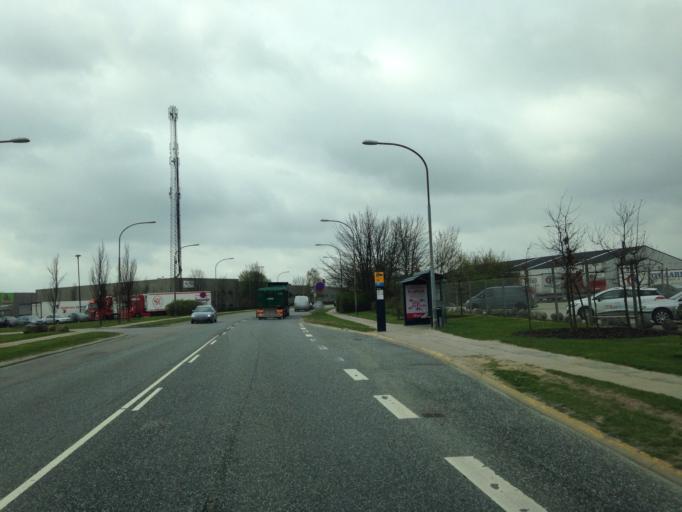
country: DK
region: Capital Region
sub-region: Ishoj Kommune
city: Ishoj
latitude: 55.6203
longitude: 12.3353
